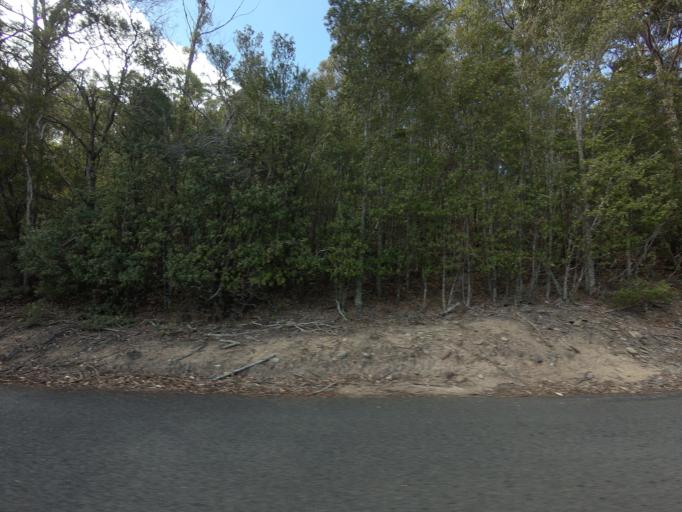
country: AU
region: Tasmania
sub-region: Break O'Day
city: St Helens
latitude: -41.6313
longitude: 148.2334
